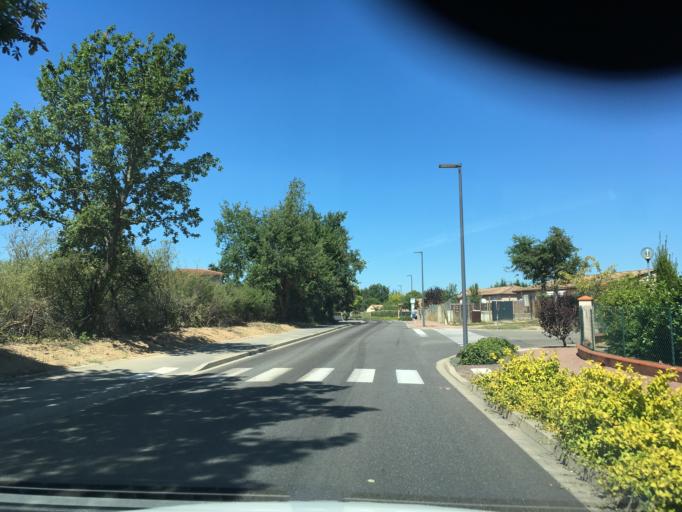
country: FR
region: Midi-Pyrenees
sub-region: Departement du Tarn-et-Garonne
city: Montauban
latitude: 44.0320
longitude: 1.3421
